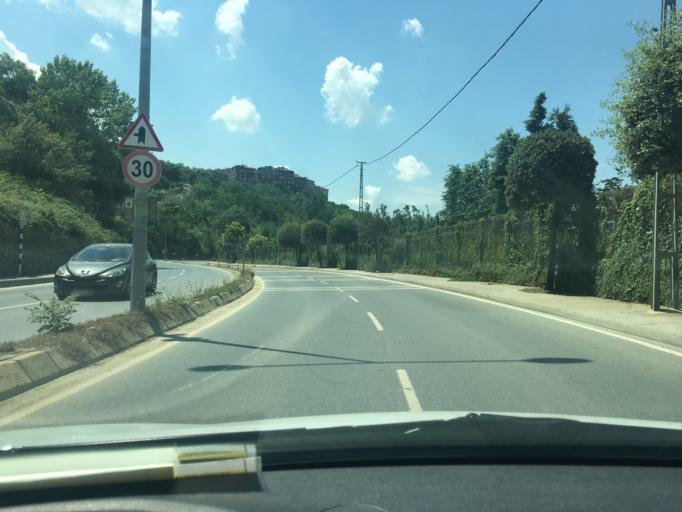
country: TR
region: Istanbul
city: Sultangazi
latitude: 41.0905
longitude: 28.9302
